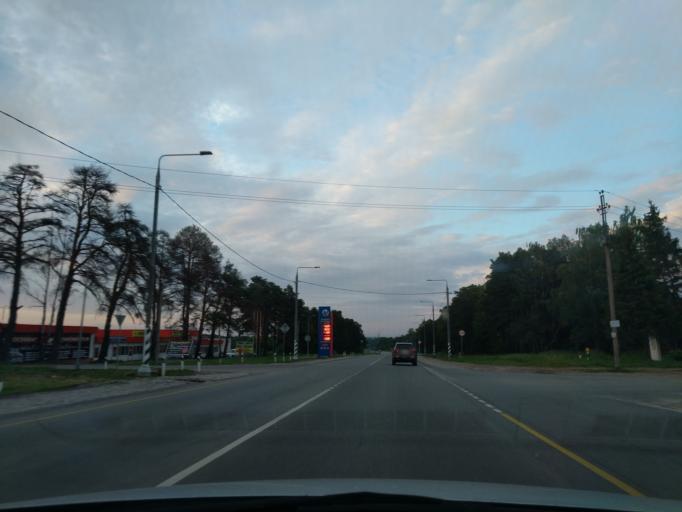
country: RU
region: Kaluga
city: Maloyaroslavets
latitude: 55.0207
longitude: 36.5000
